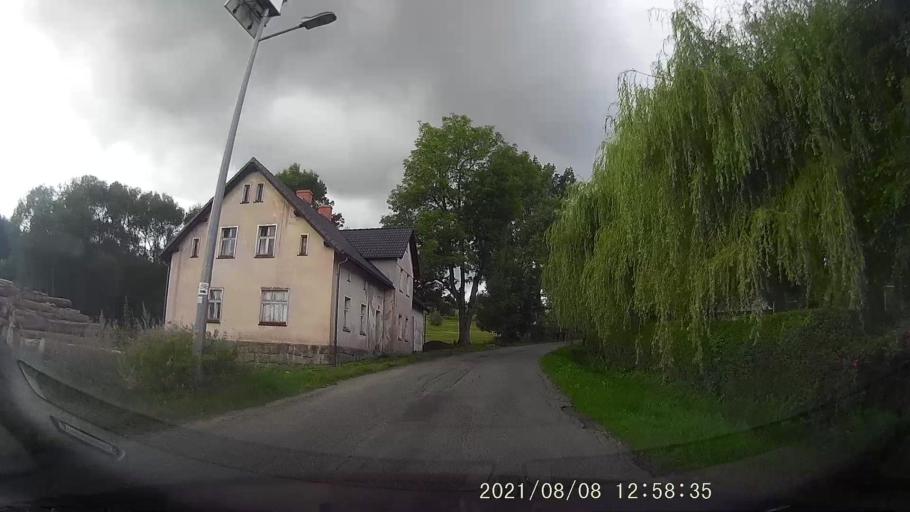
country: PL
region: Lower Silesian Voivodeship
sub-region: Powiat klodzki
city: Duszniki-Zdroj
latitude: 50.4084
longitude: 16.3579
